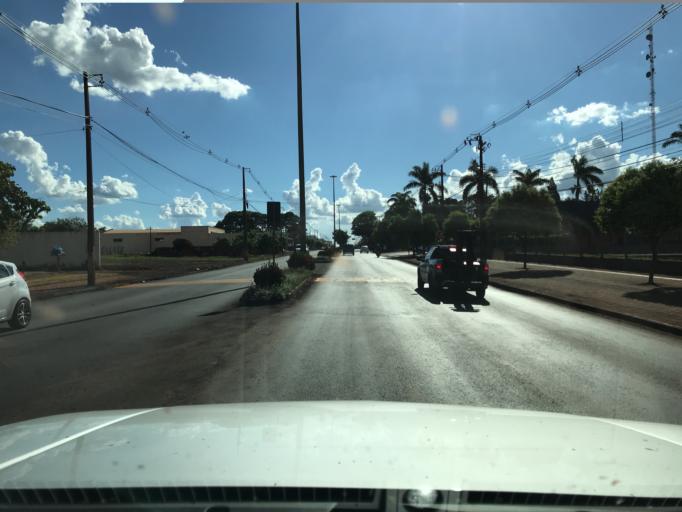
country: BR
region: Parana
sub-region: Palotina
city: Palotina
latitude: -24.2809
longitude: -53.8316
